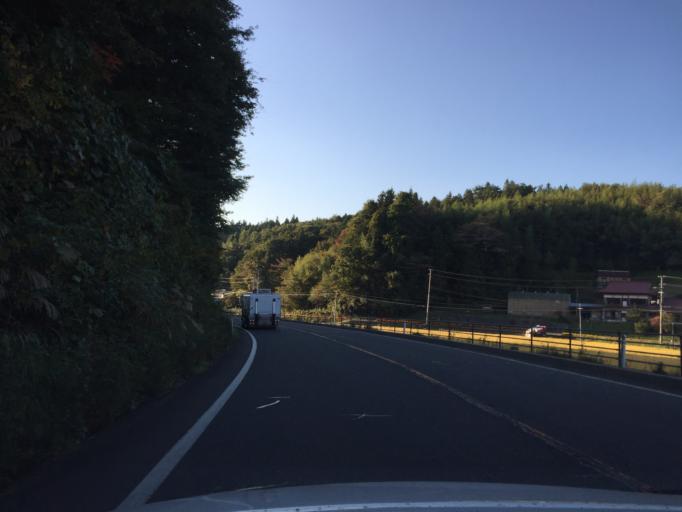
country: JP
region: Fukushima
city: Ishikawa
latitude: 37.2209
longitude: 140.5900
